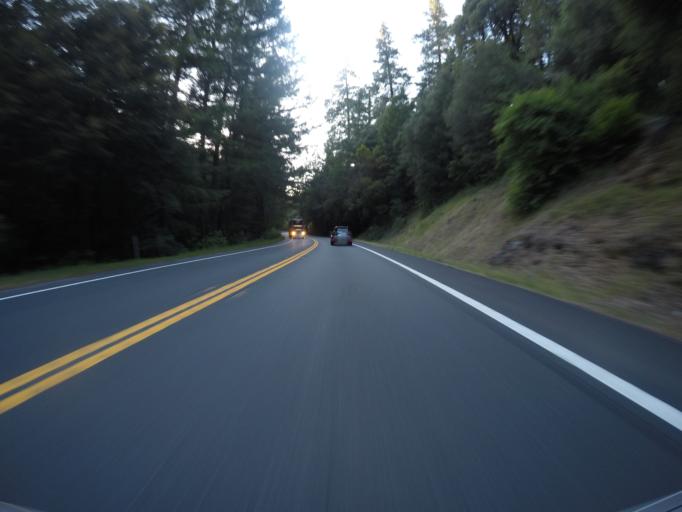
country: US
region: California
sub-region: Mendocino County
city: Laytonville
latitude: 39.8044
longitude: -123.5443
